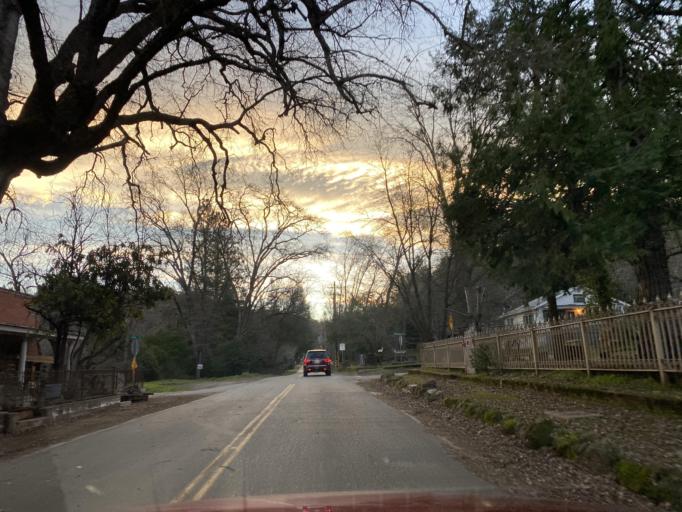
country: US
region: California
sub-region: Amador County
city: Plymouth
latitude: 38.5039
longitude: -120.7570
